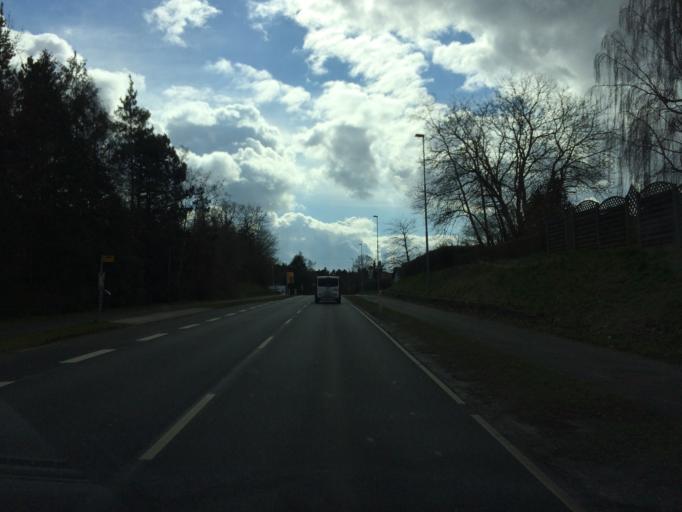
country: DK
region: South Denmark
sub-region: Nordfyns Kommune
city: Sonderso
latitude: 55.4153
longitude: 10.2696
